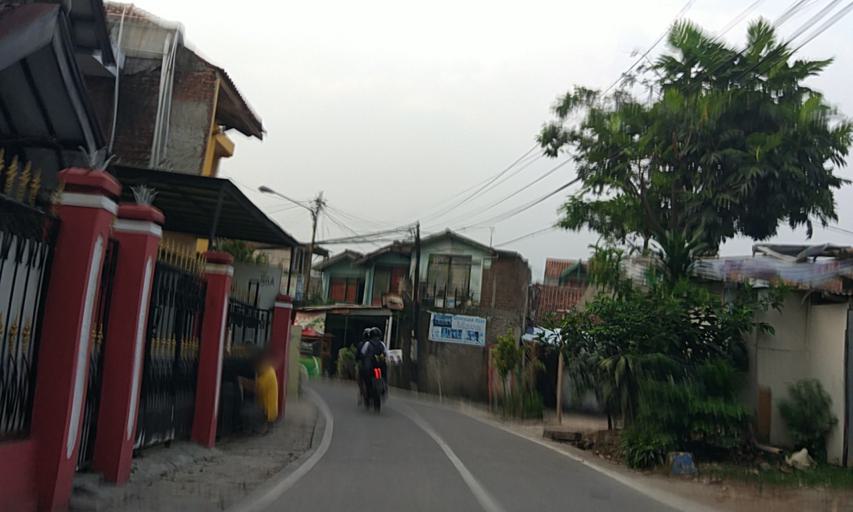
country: ID
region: West Java
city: Bandung
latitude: -6.9134
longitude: 107.6833
